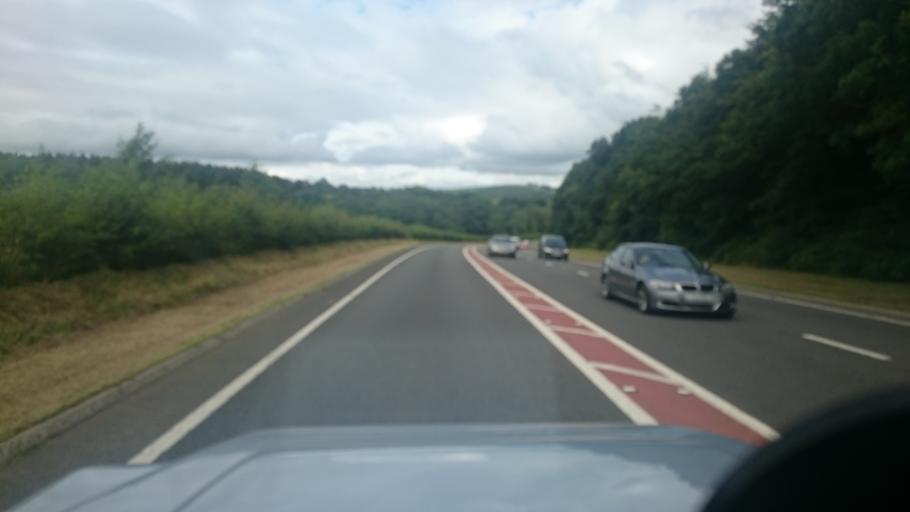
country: GB
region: Wales
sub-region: Pembrokeshire
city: Wiston
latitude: 51.8020
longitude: -4.8155
